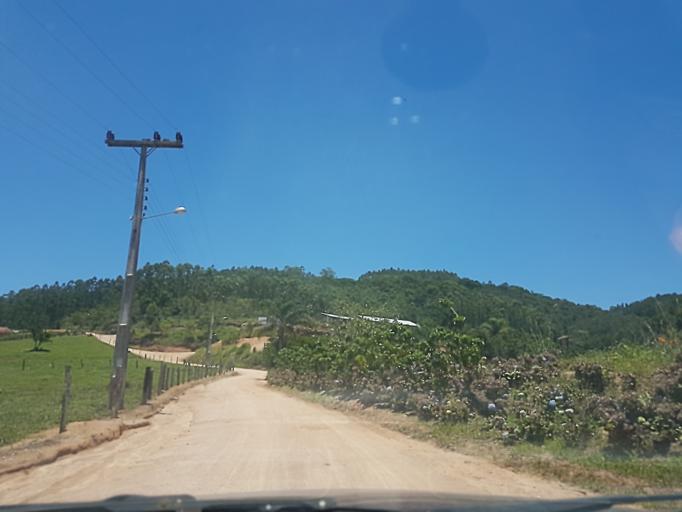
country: BR
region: Santa Catarina
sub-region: Braco Do Norte
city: Braco do Norte
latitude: -28.3879
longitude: -49.1294
